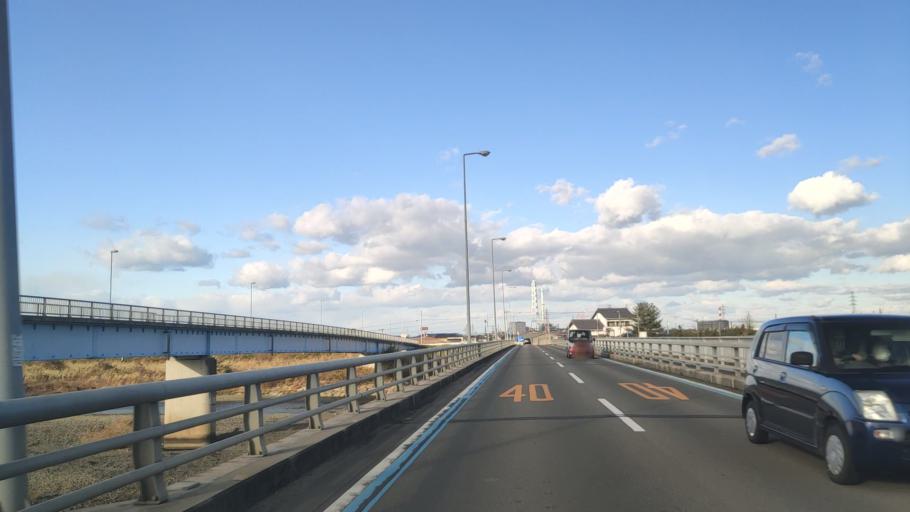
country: JP
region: Ehime
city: Saijo
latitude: 33.9123
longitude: 133.1615
